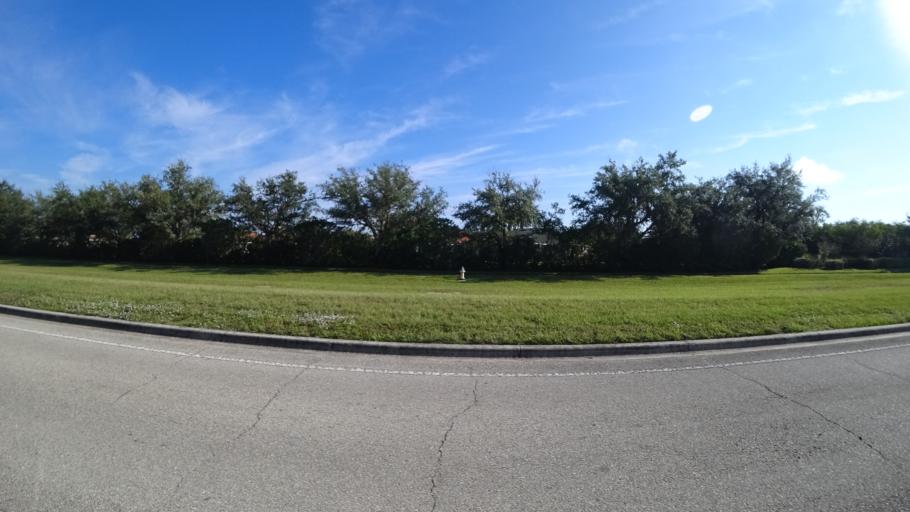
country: US
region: Florida
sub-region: Sarasota County
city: Desoto Lakes
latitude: 27.4160
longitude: -82.4746
